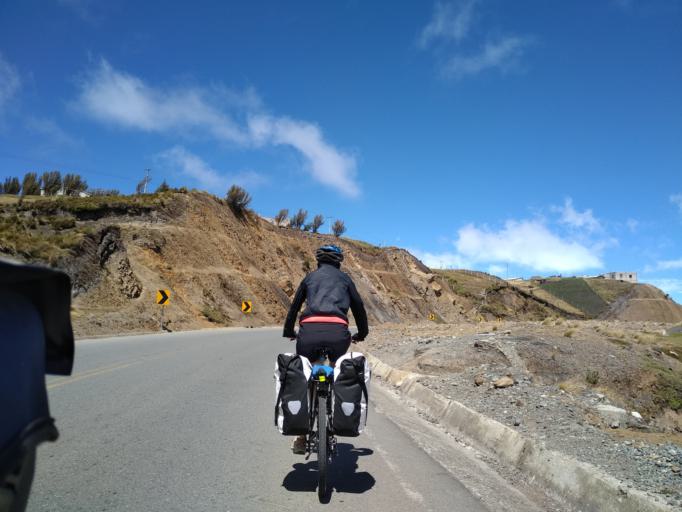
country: EC
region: Cotopaxi
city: Pujili
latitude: -0.9676
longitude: -78.9273
